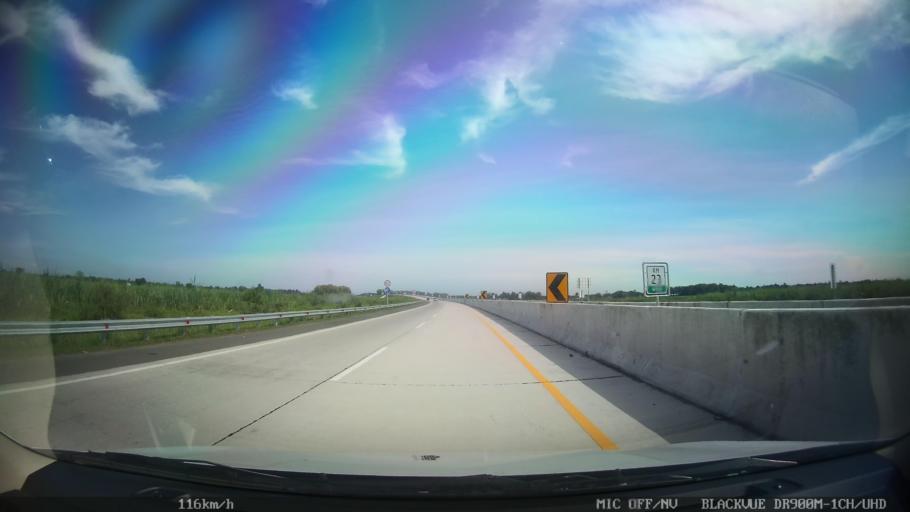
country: ID
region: North Sumatra
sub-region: Kabupaten Langkat
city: Stabat
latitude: 3.6955
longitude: 98.5406
